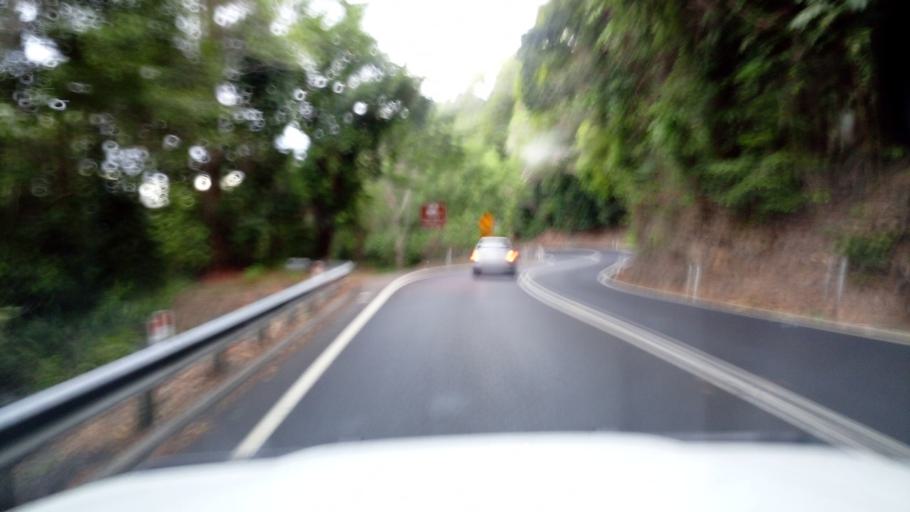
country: AU
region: Queensland
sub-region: Tablelands
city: Kuranda
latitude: -16.8333
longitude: 145.6704
